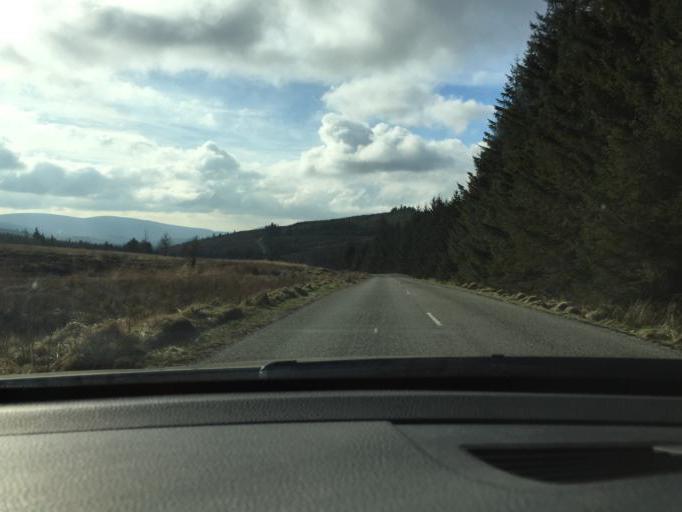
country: IE
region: Leinster
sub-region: Wicklow
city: Valleymount
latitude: 53.0568
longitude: -6.4147
